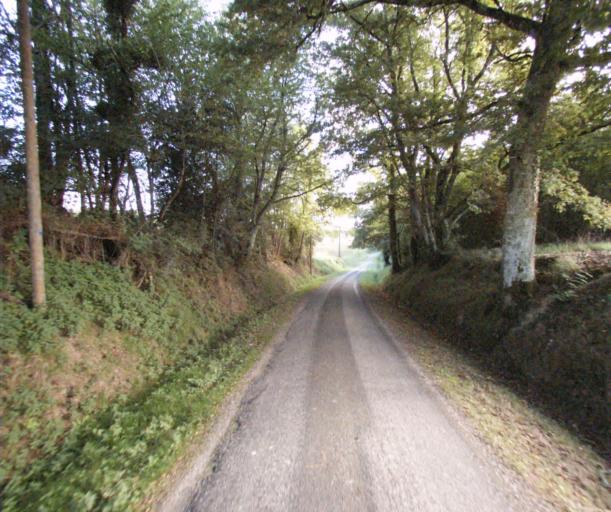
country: FR
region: Midi-Pyrenees
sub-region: Departement du Gers
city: Cazaubon
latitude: 43.8920
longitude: 0.0038
